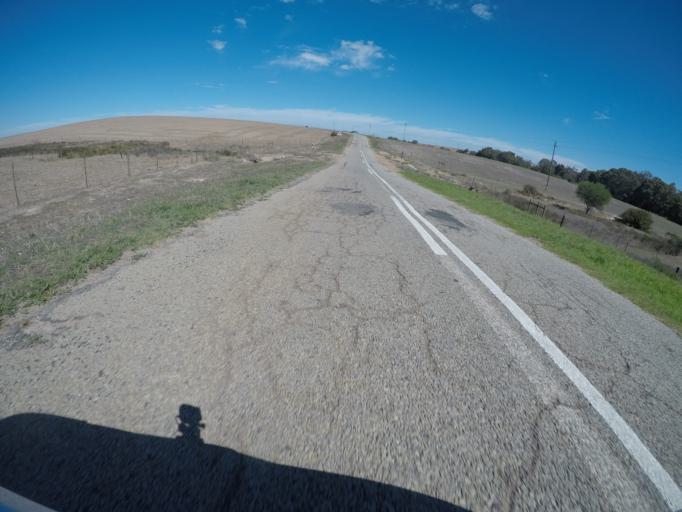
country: ZA
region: Western Cape
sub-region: City of Cape Town
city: Atlantis
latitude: -33.6178
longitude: 18.6336
